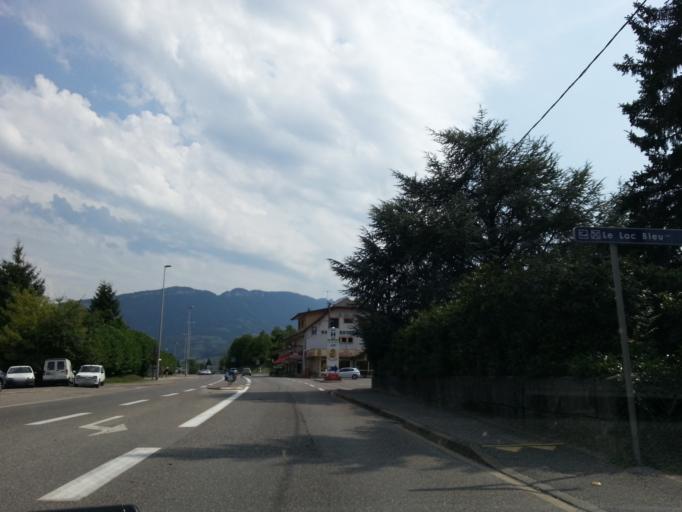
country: FR
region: Rhone-Alpes
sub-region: Departement de la Haute-Savoie
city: Sevrier
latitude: 45.8484
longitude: 6.1460
